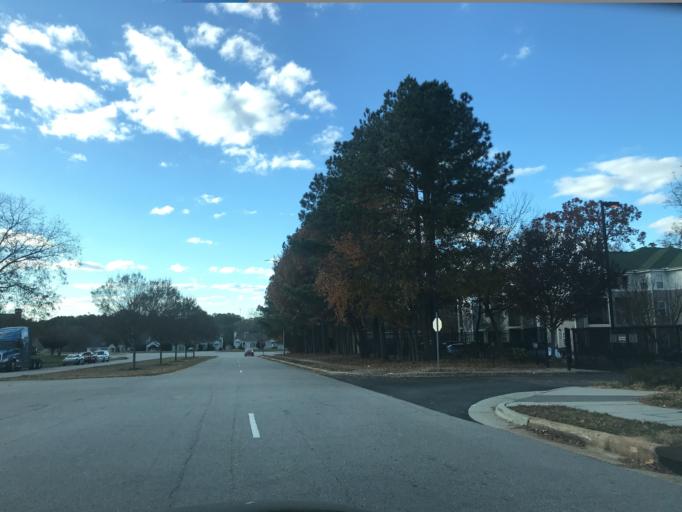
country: US
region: North Carolina
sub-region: Wake County
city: Raleigh
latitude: 35.8461
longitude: -78.5891
